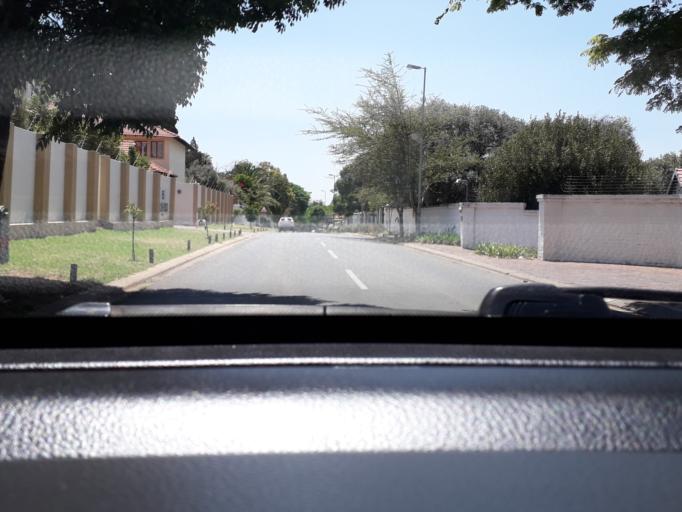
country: ZA
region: Gauteng
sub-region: City of Johannesburg Metropolitan Municipality
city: Midrand
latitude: -26.0504
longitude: 28.0629
